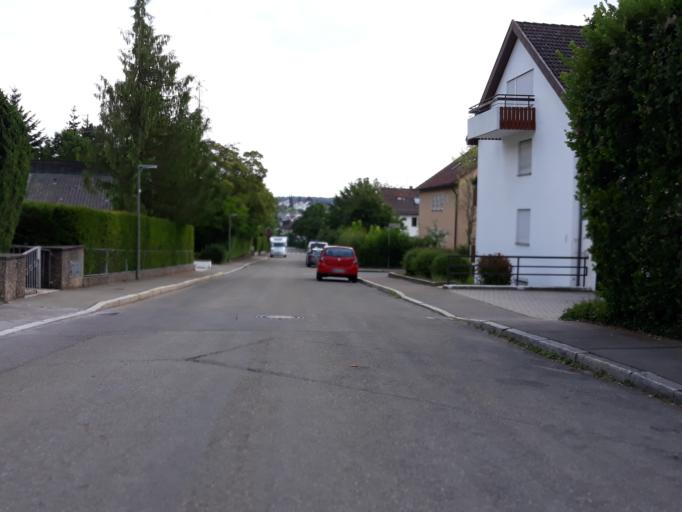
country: DE
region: Baden-Wuerttemberg
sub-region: Regierungsbezirk Stuttgart
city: Boeblingen
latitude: 48.6855
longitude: 9.0334
